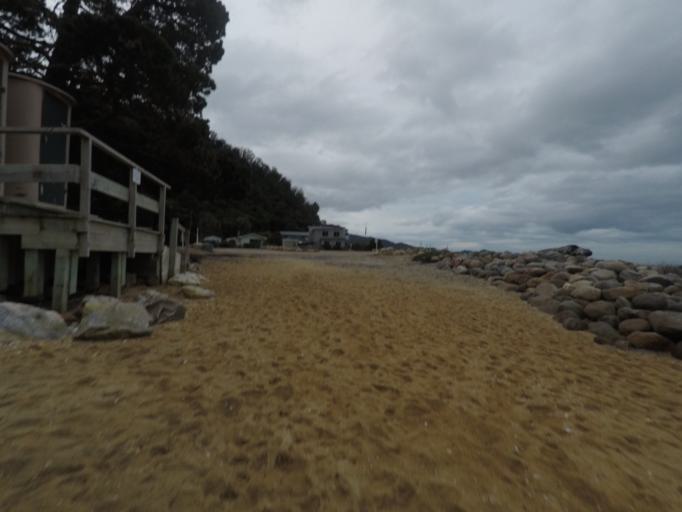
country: NZ
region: Tasman
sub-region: Tasman District
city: Motueka
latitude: -41.0095
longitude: 173.0076
